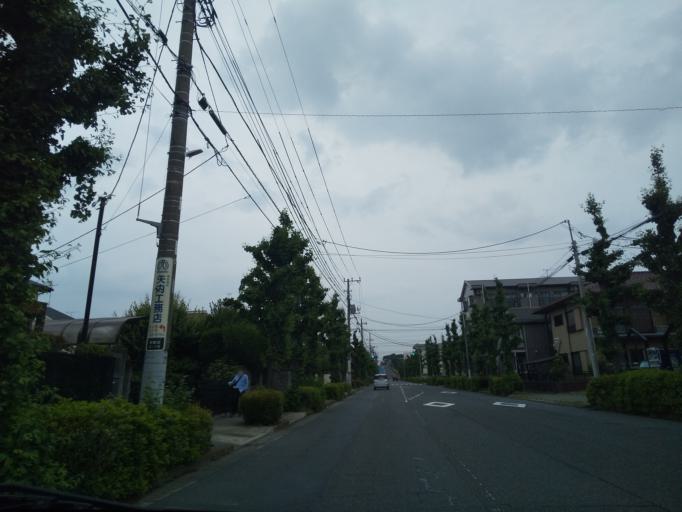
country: JP
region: Tokyo
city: Hino
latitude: 35.6642
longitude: 139.3903
